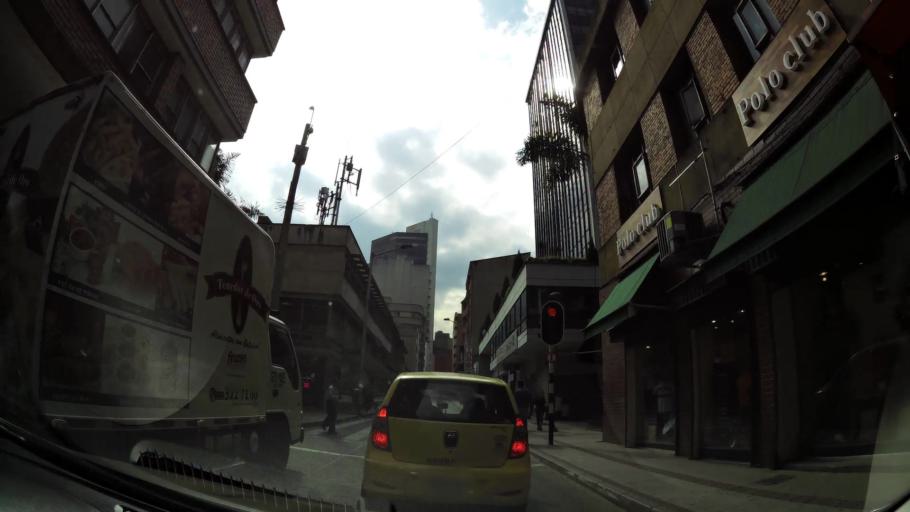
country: CO
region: Antioquia
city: Medellin
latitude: 6.2521
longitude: -75.5661
